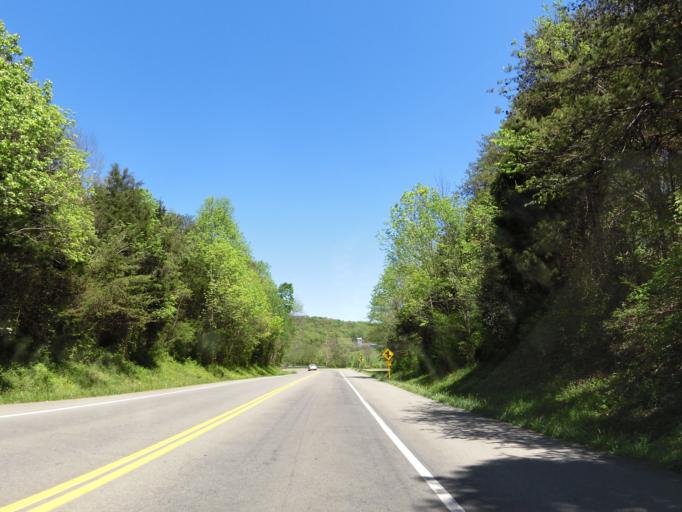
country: US
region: Tennessee
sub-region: Greene County
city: Mosheim
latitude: 36.0771
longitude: -82.9612
